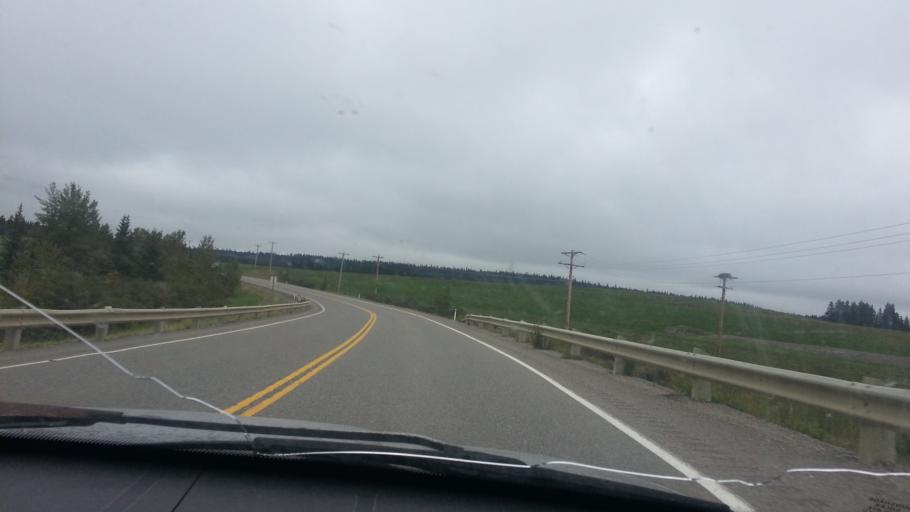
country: CA
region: Alberta
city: Cochrane
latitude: 51.1208
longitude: -114.6983
